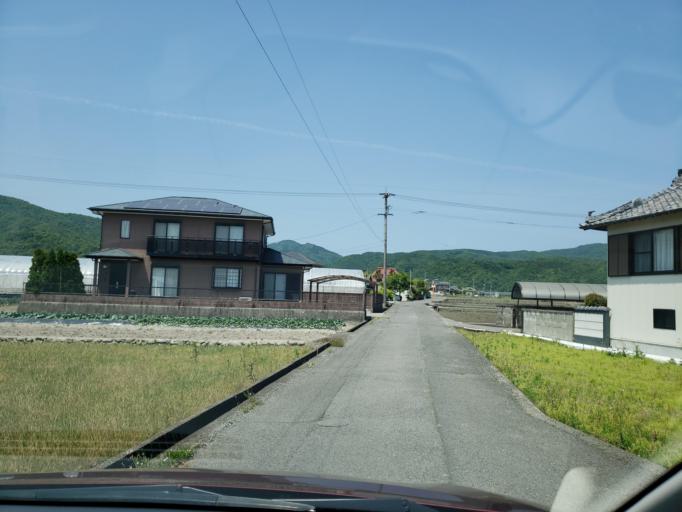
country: JP
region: Tokushima
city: Kamojimacho-jogejima
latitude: 34.0957
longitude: 134.2682
